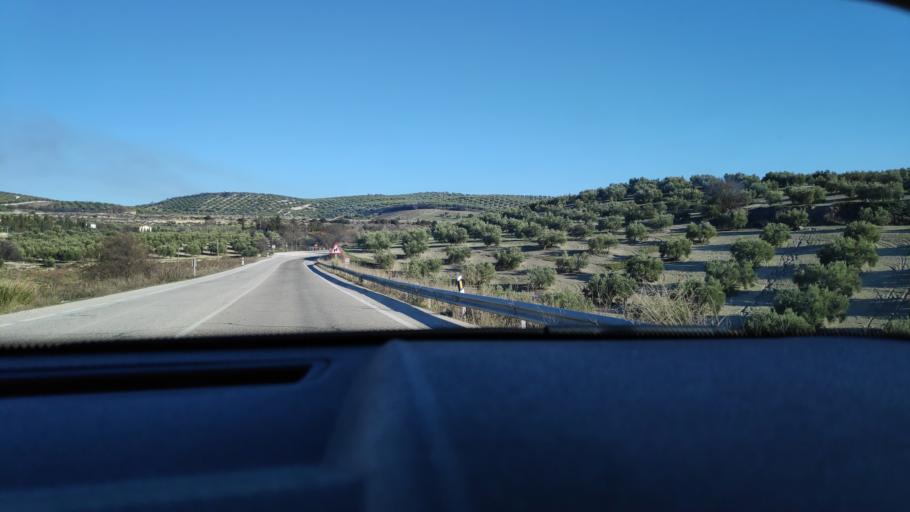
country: ES
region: Andalusia
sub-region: Province of Cordoba
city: Baena
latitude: 37.6005
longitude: -4.3098
